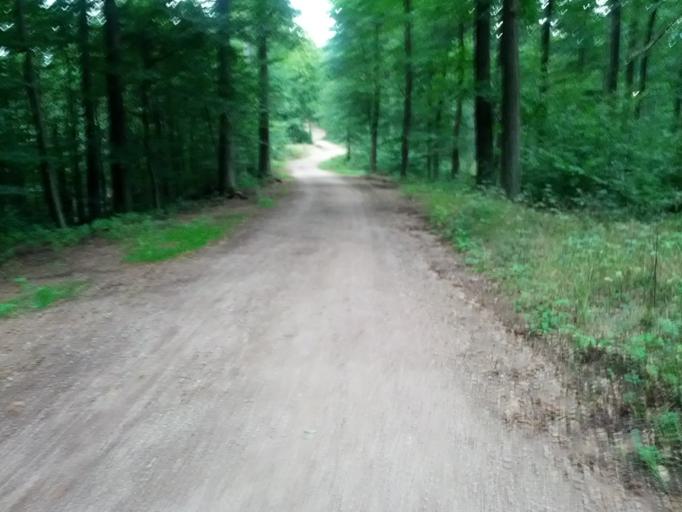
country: DE
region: Thuringia
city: Wolfsburg-Unkeroda
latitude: 50.9427
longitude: 10.2906
